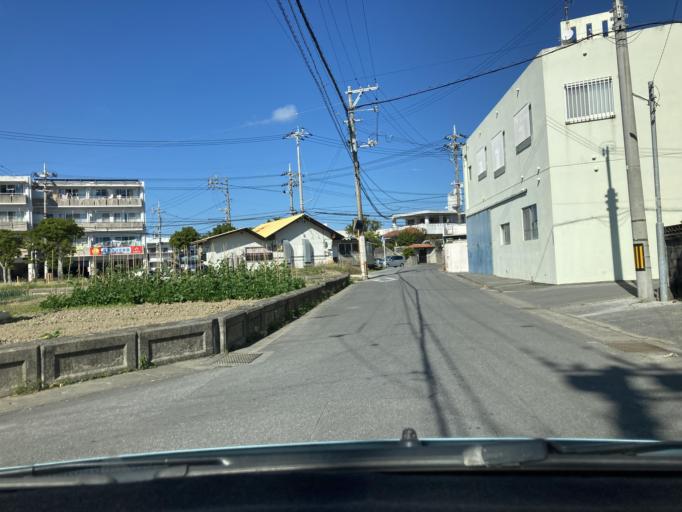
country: JP
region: Okinawa
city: Okinawa
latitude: 26.3457
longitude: 127.8323
